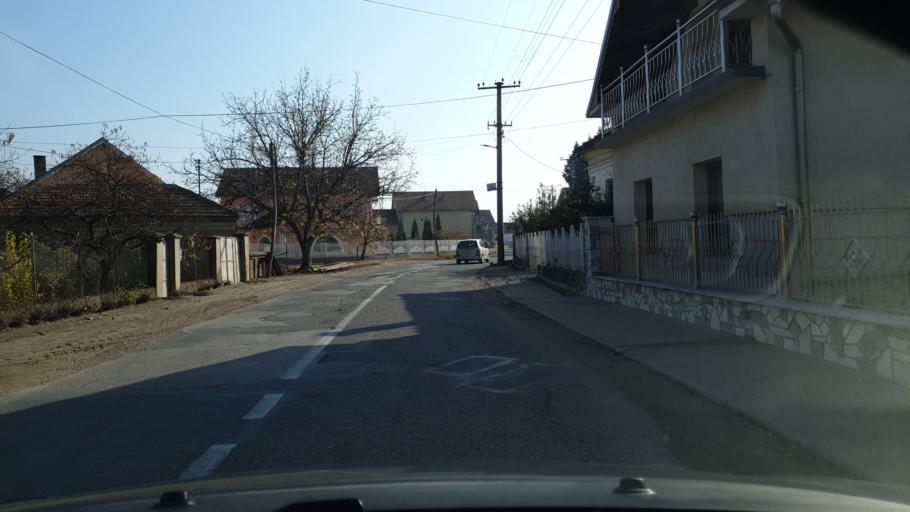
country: RS
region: Central Serbia
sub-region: Borski Okrug
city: Negotin
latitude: 44.1978
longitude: 22.5886
